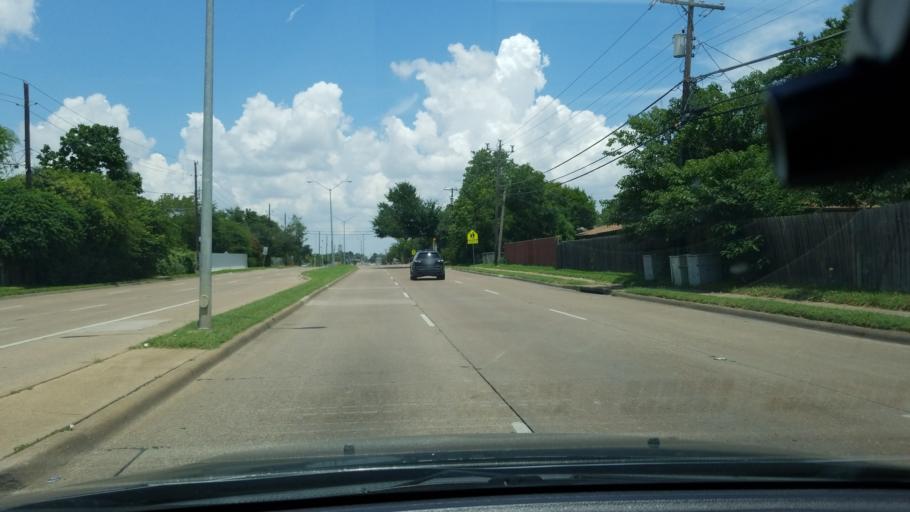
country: US
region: Texas
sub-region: Dallas County
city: Balch Springs
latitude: 32.7382
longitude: -96.6483
